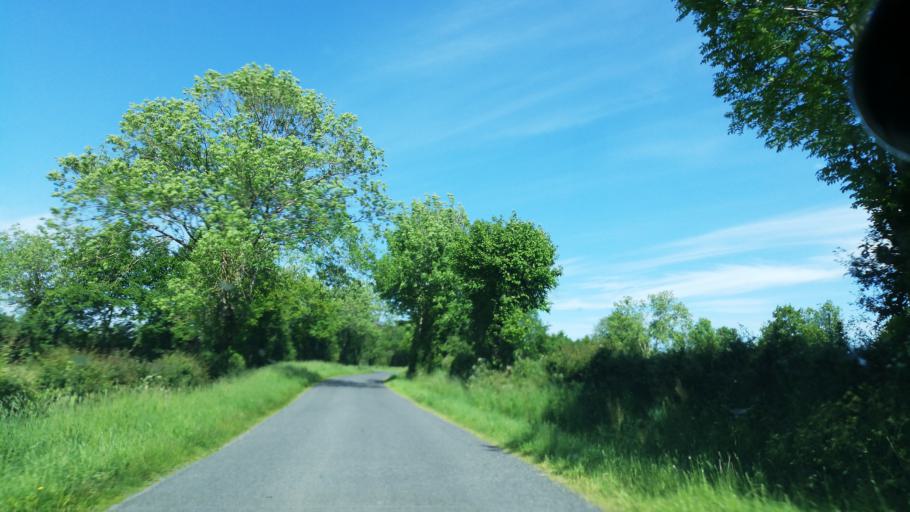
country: FR
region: Poitou-Charentes
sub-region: Departement des Deux-Sevres
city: Moncoutant
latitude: 46.7023
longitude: -0.5787
